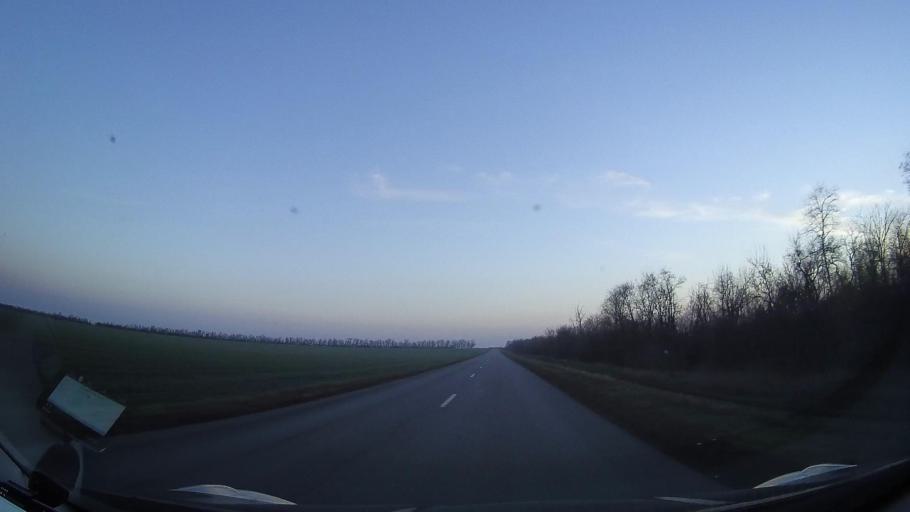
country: RU
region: Rostov
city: Zernograd
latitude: 46.9179
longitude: 40.3388
